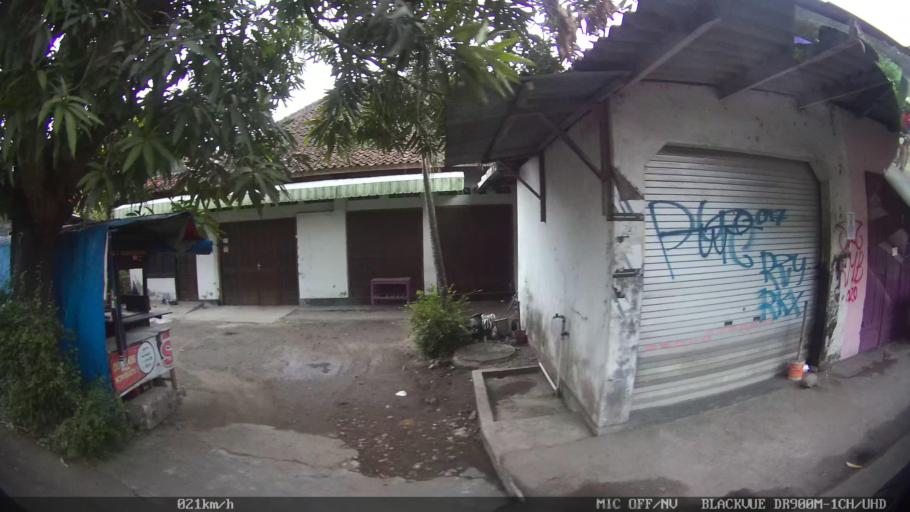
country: ID
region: Daerah Istimewa Yogyakarta
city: Depok
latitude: -7.8295
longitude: 110.4139
